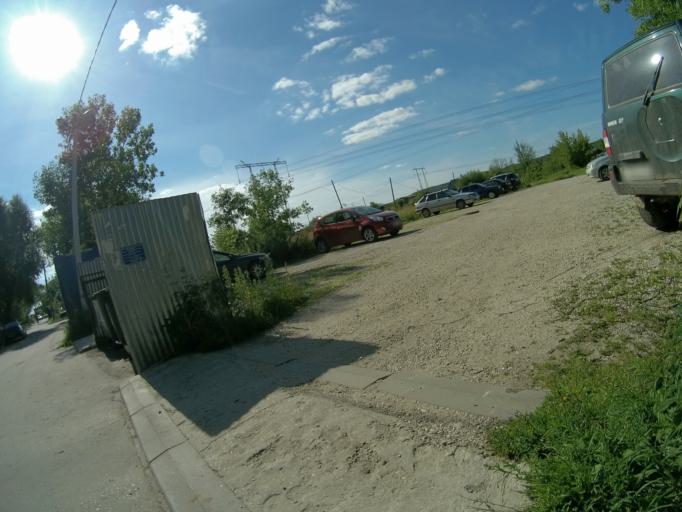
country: RU
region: Vladimir
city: Vorsha
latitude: 56.0980
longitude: 40.1939
